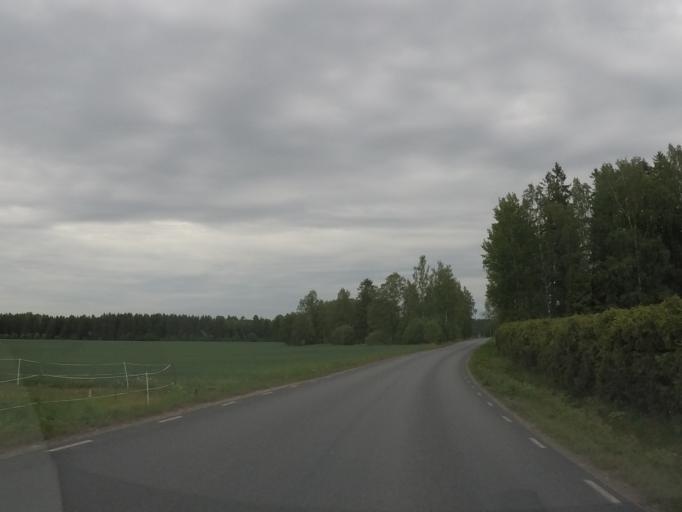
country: SE
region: Soedermanland
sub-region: Eskilstuna Kommun
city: Arla
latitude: 59.2708
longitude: 16.6622
